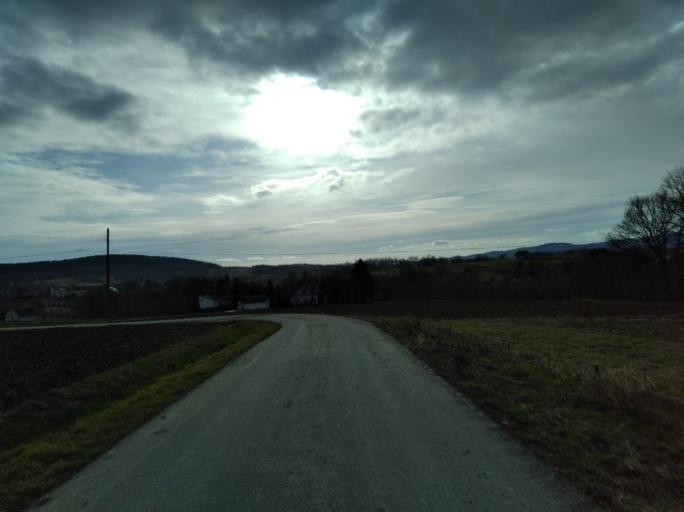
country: PL
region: Subcarpathian Voivodeship
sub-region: Powiat strzyzowski
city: Strzyzow
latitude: 49.8510
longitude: 21.7744
